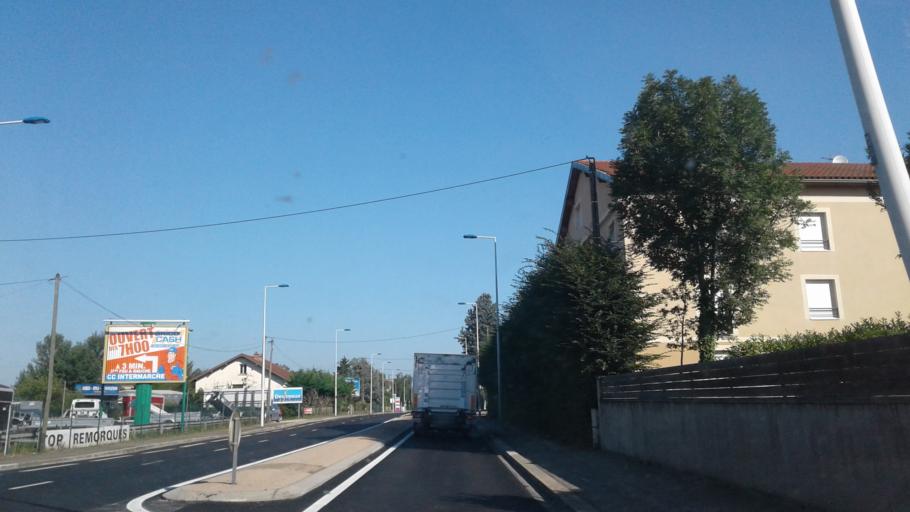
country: FR
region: Rhone-Alpes
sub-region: Departement de l'Ain
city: Bourg-en-Bresse
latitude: 46.1890
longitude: 5.2441
